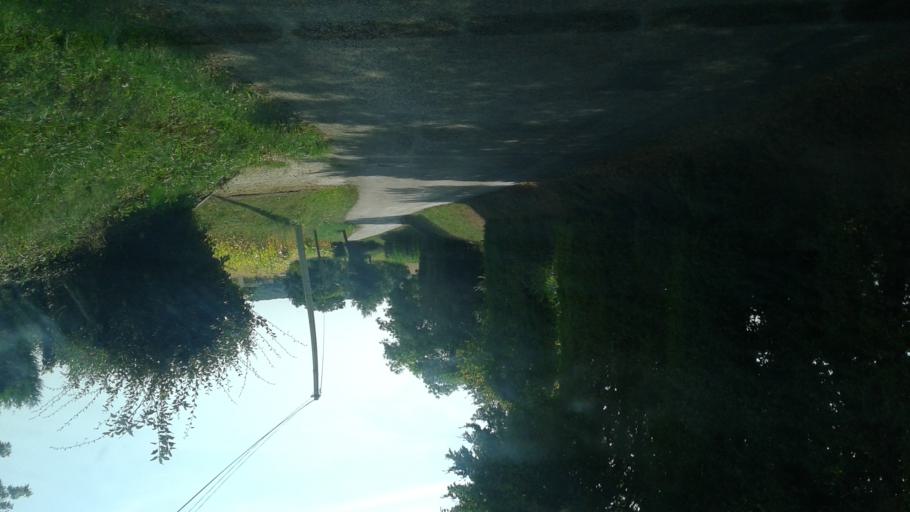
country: FR
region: Rhone-Alpes
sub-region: Departement de l'Ain
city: Tramoyes
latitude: 45.8684
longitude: 4.9756
